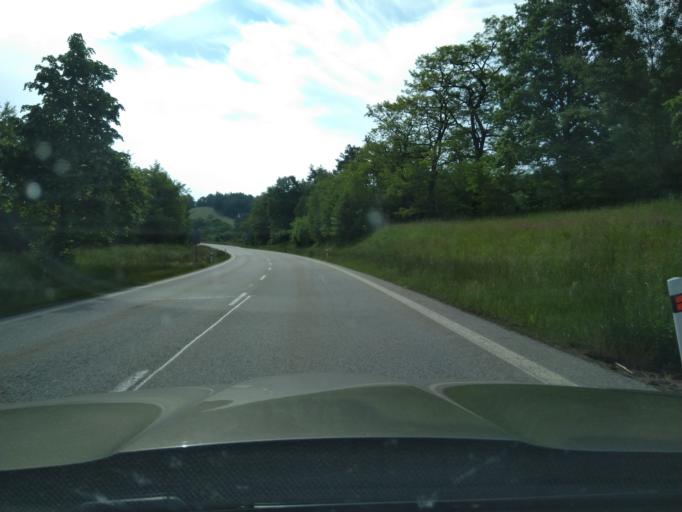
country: CZ
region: Jihocesky
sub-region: Okres Prachatice
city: Strunkovice nad Blanici
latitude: 49.0542
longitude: 14.0525
